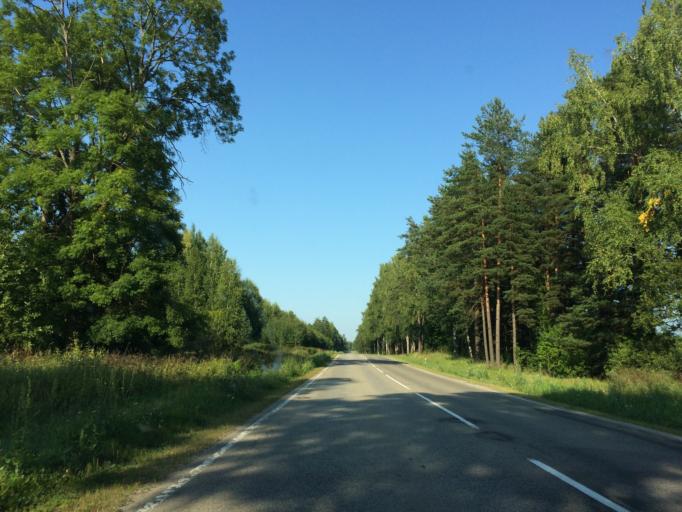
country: LV
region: Ludzas Rajons
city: Ludza
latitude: 56.5336
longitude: 27.5533
